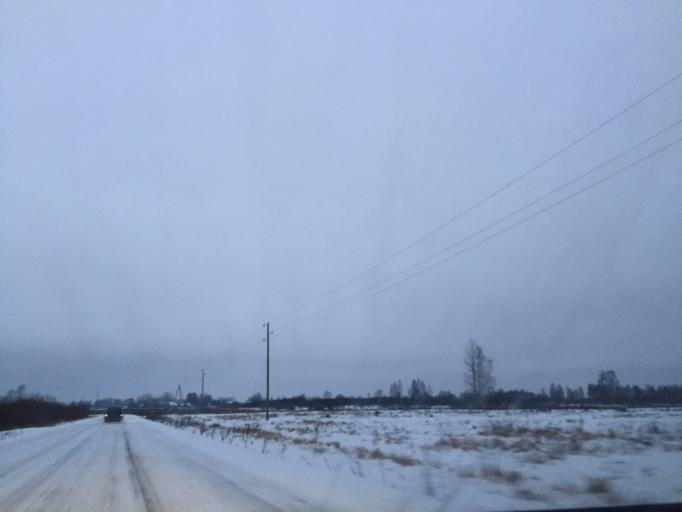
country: LV
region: Raunas
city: Rauna
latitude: 57.4295
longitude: 25.6335
